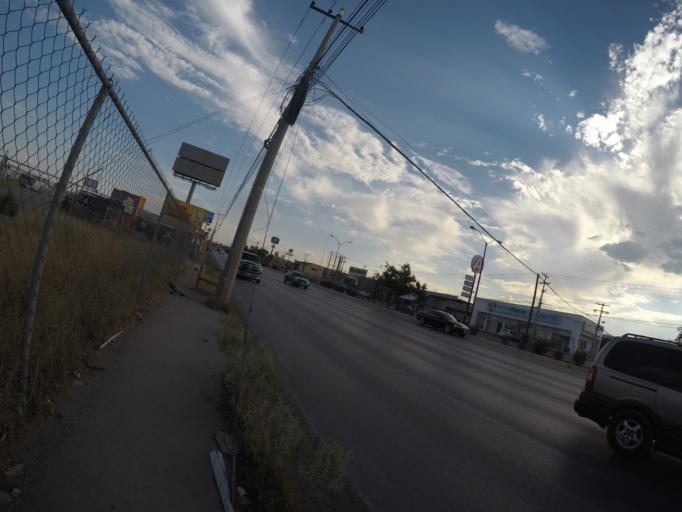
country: MX
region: Chihuahua
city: Ciudad Juarez
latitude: 31.6953
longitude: -106.4243
